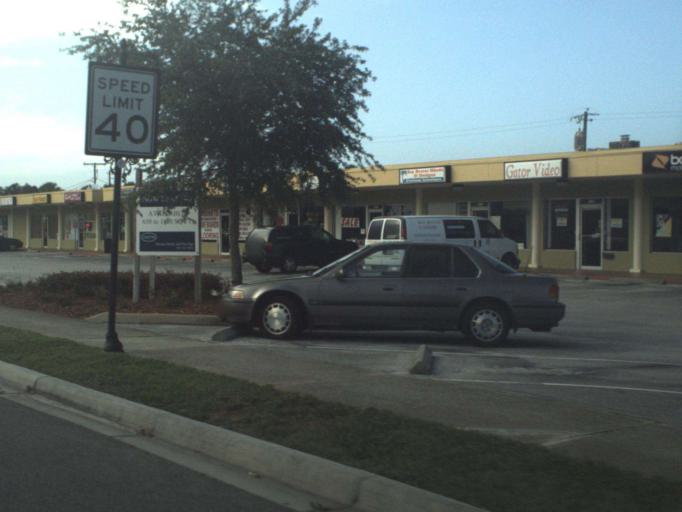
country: US
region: Florida
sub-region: Volusia County
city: South Daytona
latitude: 29.1691
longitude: -81.0004
